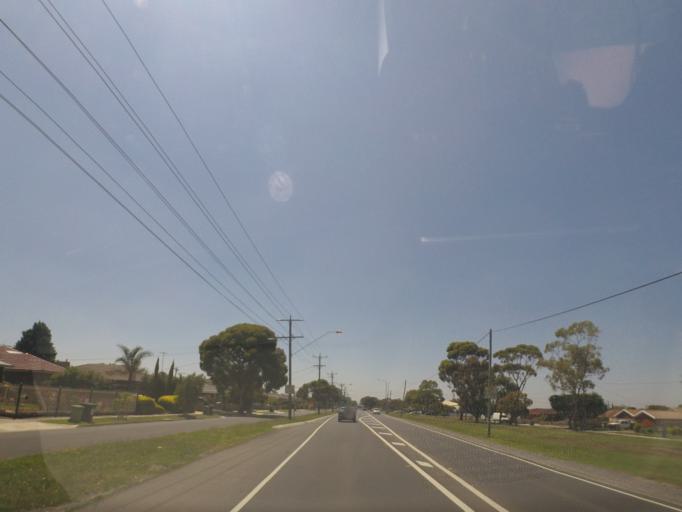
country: AU
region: Victoria
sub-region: Hume
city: Craigieburn
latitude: -37.5975
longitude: 144.9284
